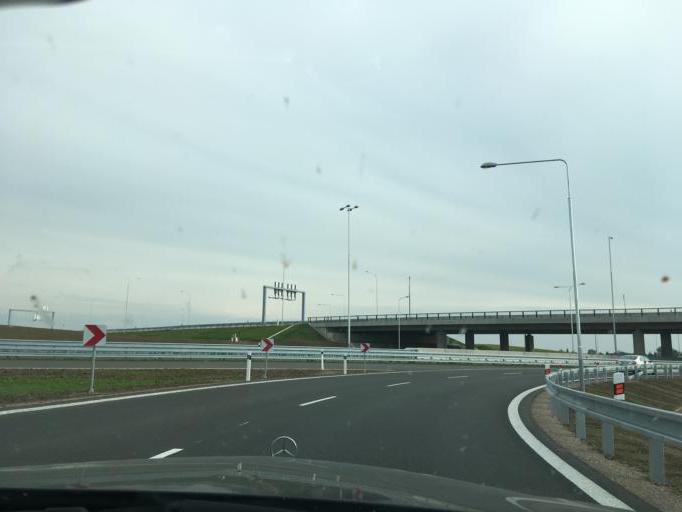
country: CZ
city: Stezery
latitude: 50.2023
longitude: 15.7668
